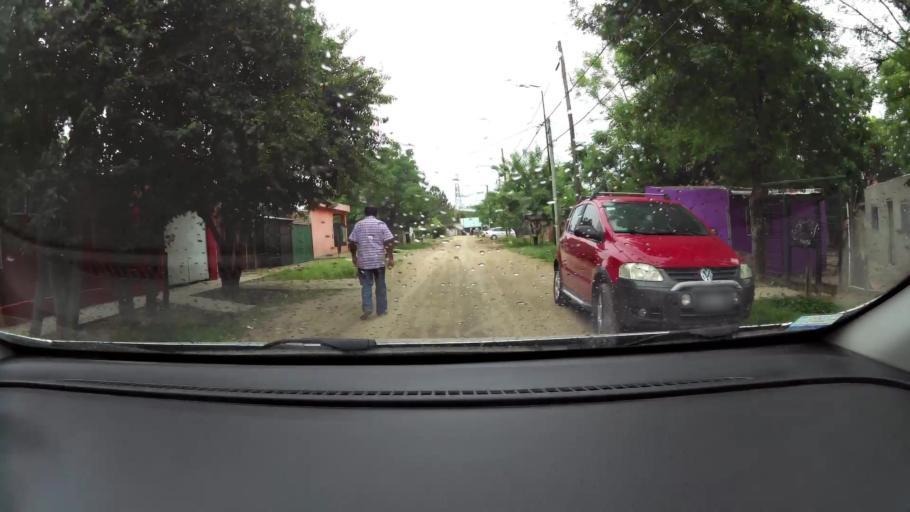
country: AR
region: Buenos Aires
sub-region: Partido de Zarate
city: Zarate
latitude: -34.1153
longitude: -59.0392
